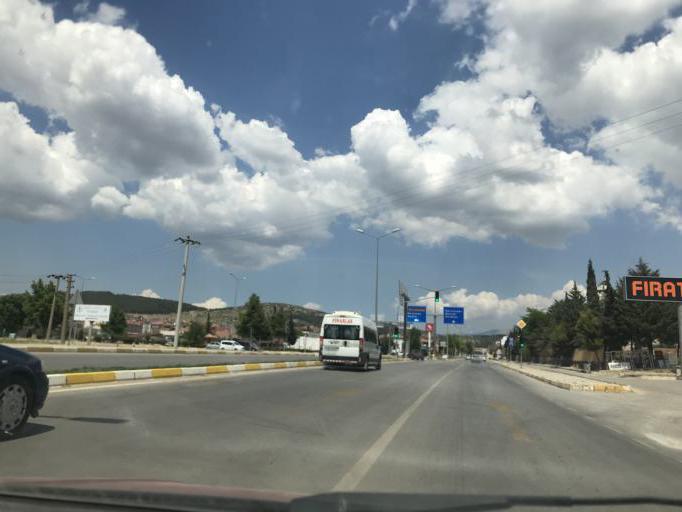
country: TR
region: Denizli
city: Tavas
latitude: 37.5636
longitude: 29.0628
